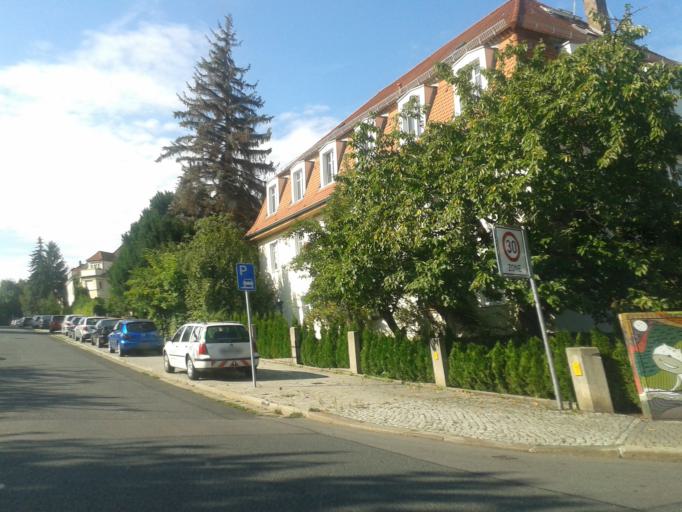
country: DE
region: Saxony
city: Dresden
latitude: 51.0192
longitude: 13.7578
